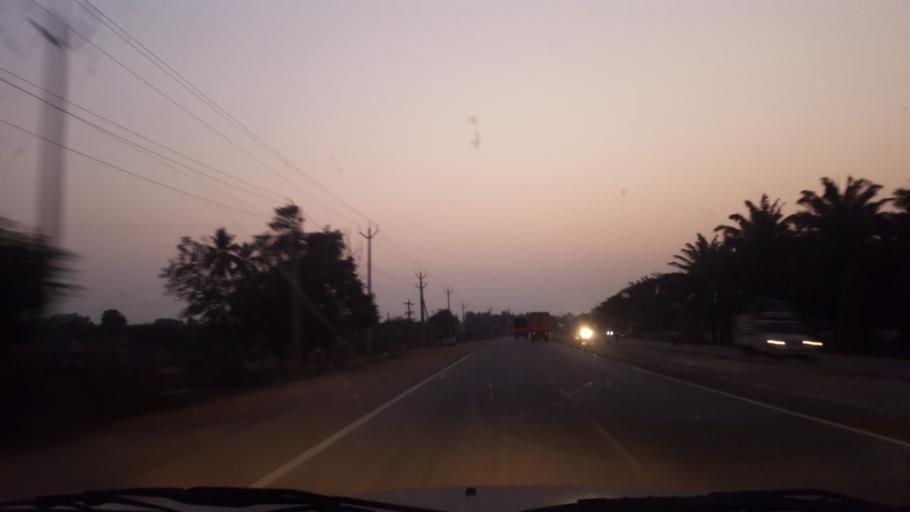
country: IN
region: Andhra Pradesh
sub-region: East Godavari
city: Peddapuram
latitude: 17.1381
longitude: 81.9704
